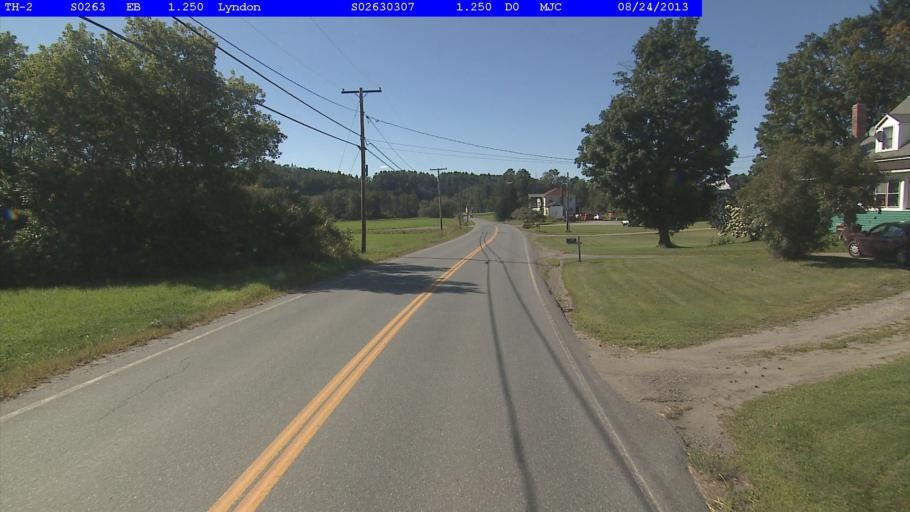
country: US
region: Vermont
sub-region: Caledonia County
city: Lyndon
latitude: 44.5048
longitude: -71.9858
